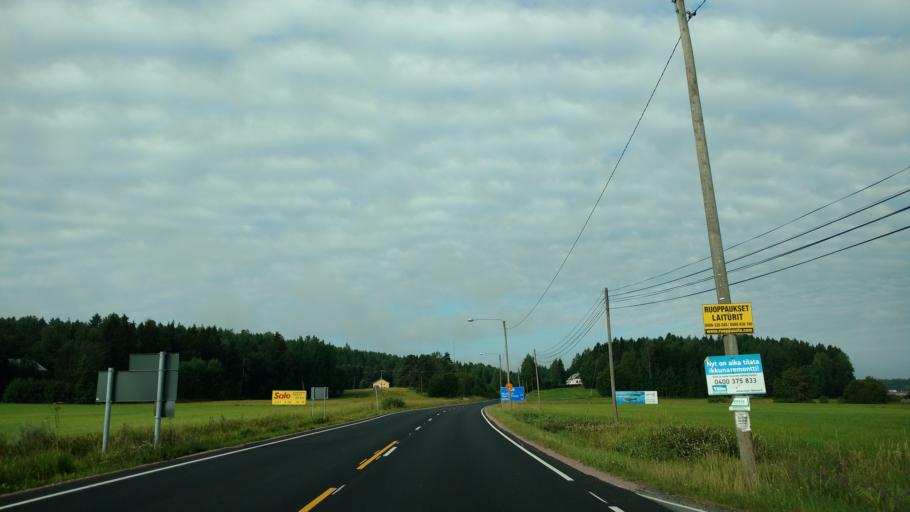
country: FI
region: Varsinais-Suomi
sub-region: Aboland-Turunmaa
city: Kimito
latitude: 60.1600
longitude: 22.7283
